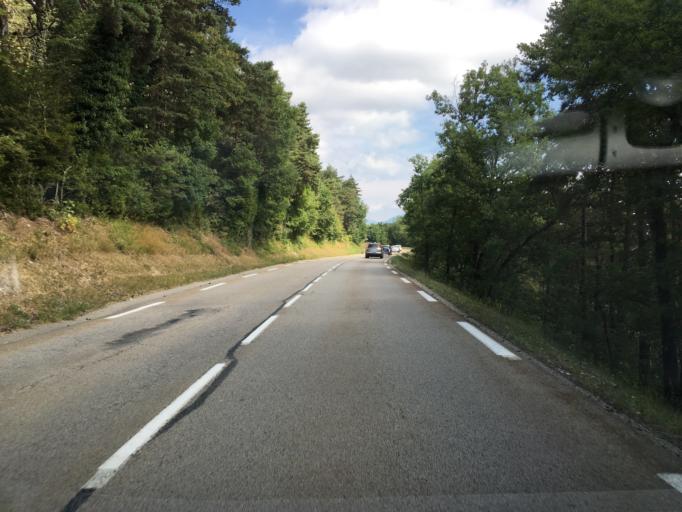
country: FR
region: Rhone-Alpes
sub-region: Departement de l'Isere
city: Mens
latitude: 44.7817
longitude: 5.6463
